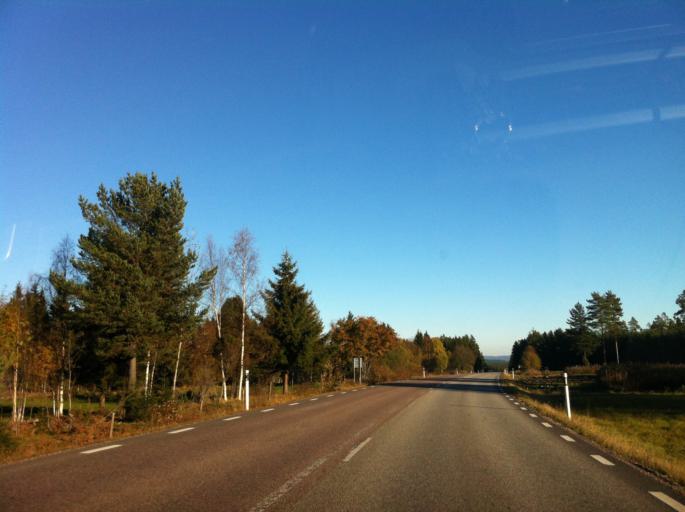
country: SE
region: Dalarna
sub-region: Leksand Municipality
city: Siljansnas
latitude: 60.9218
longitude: 14.8286
